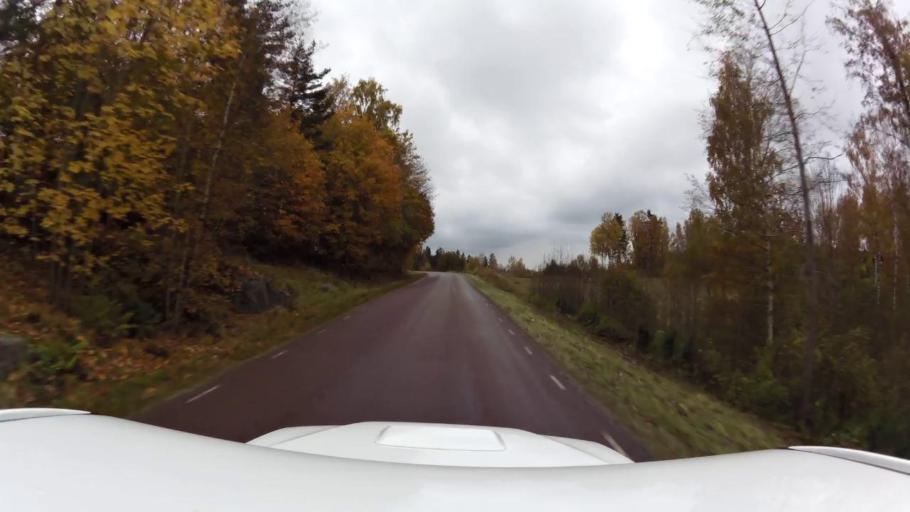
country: SE
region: OEstergoetland
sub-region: Linkopings Kommun
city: Ljungsbro
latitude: 58.5687
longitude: 15.5145
